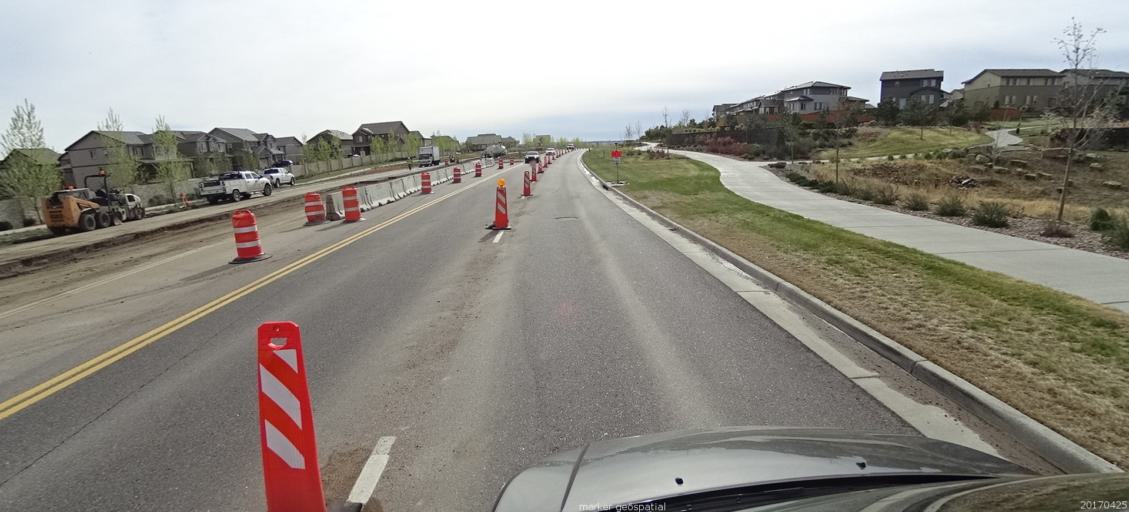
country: US
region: Colorado
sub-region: Douglas County
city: Stonegate
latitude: 39.5199
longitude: -104.8299
